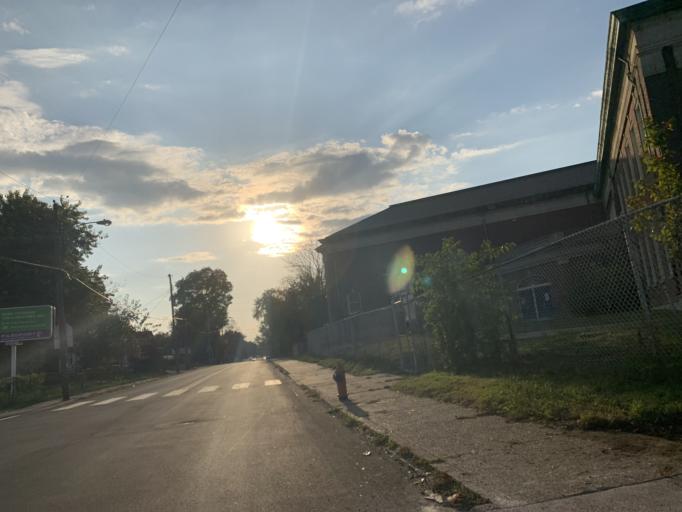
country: US
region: Kentucky
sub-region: Jefferson County
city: Louisville
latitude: 38.2348
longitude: -85.7951
